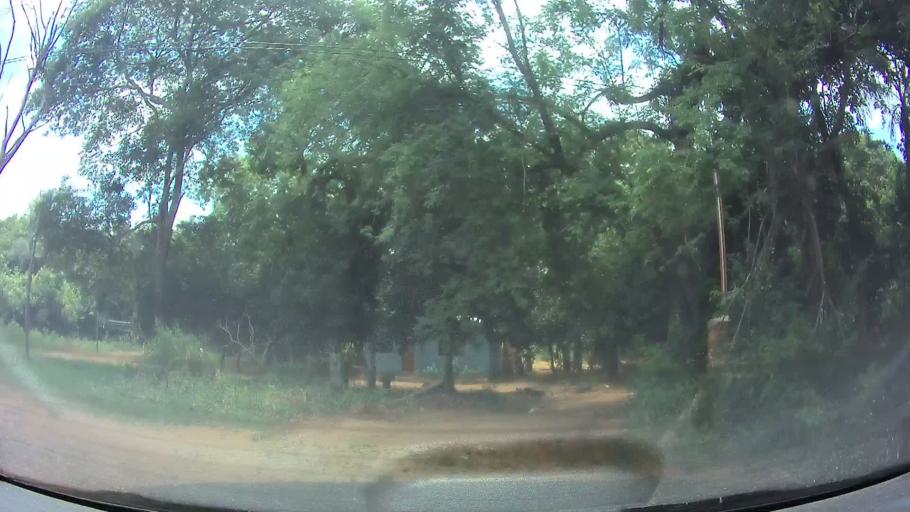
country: PY
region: Central
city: Limpio
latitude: -25.2415
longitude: -57.4472
